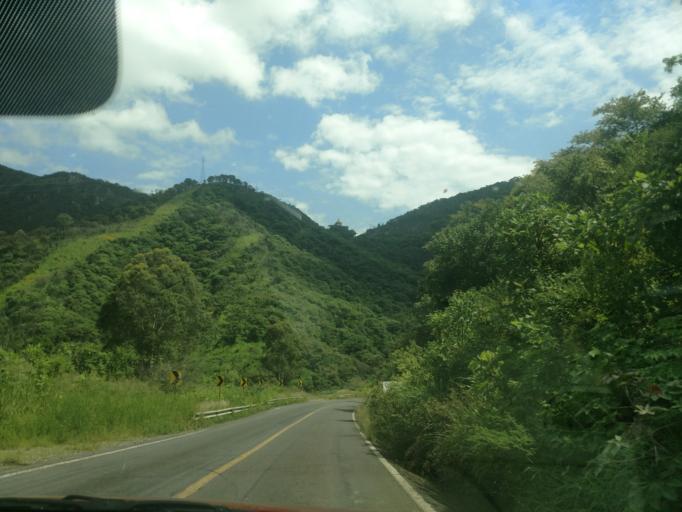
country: MX
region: Jalisco
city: Talpa de Allende
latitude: 20.4137
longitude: -104.8040
